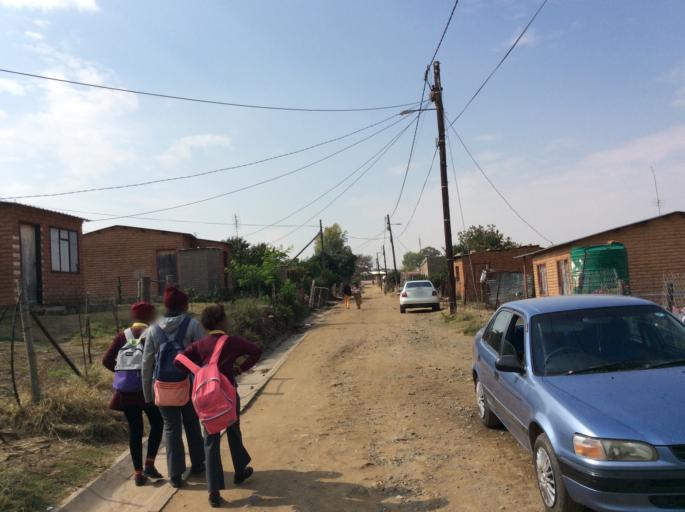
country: LS
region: Mafeteng
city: Mafeteng
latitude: -29.9835
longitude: 27.0051
